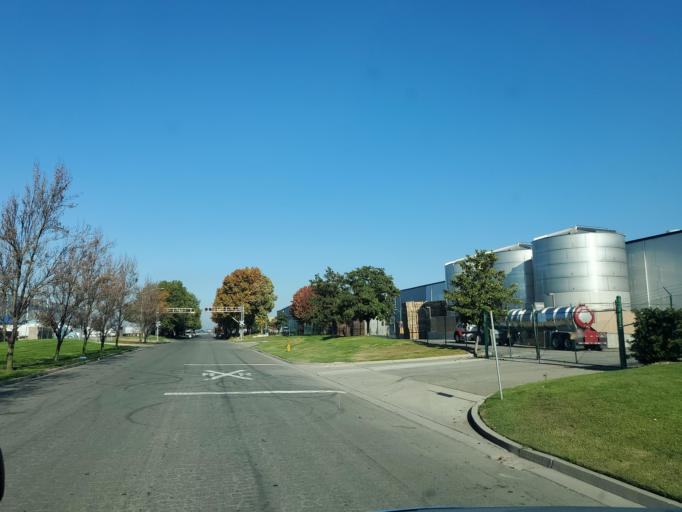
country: US
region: California
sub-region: San Joaquin County
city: Taft Mosswood
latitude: 37.9126
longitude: -121.2676
